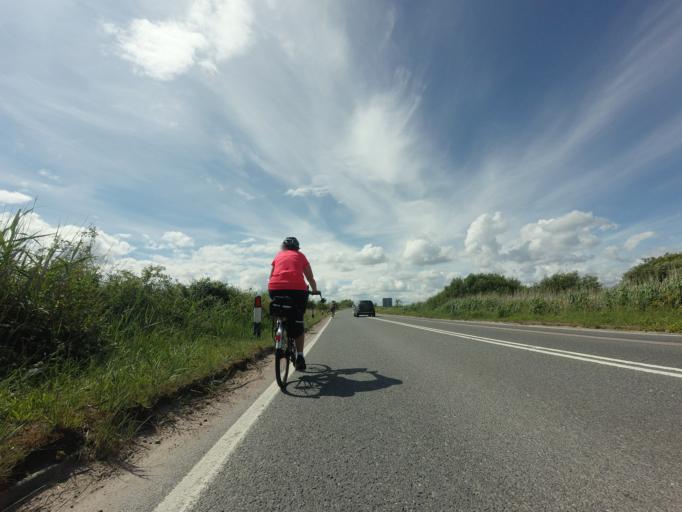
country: GB
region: England
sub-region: Medway
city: Allhallows
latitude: 51.4468
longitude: 0.6755
